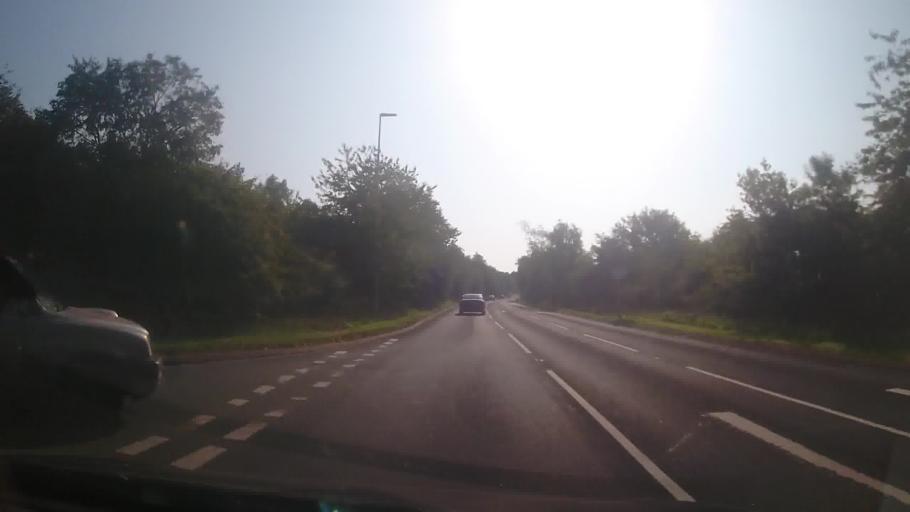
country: GB
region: England
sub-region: Shropshire
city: Bridgnorth
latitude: 52.5374
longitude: -2.4457
